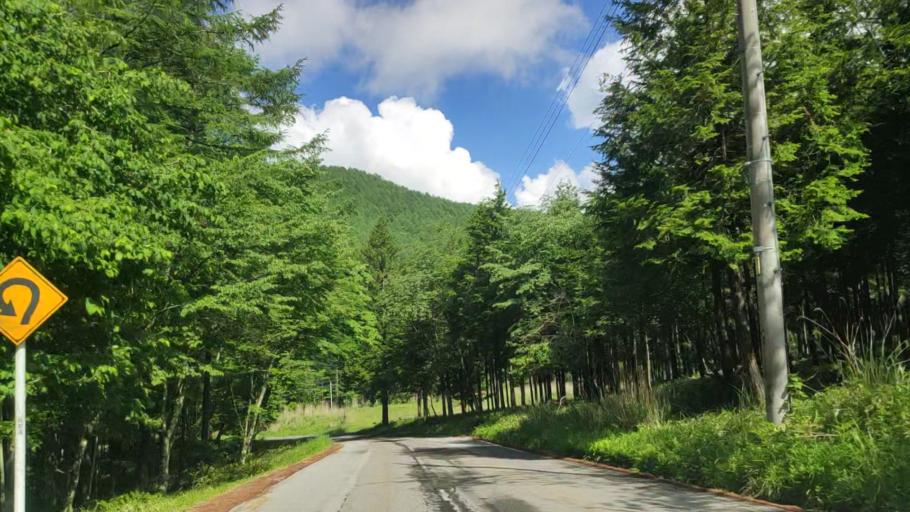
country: JP
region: Nagano
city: Suwa
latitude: 36.0889
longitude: 138.1447
